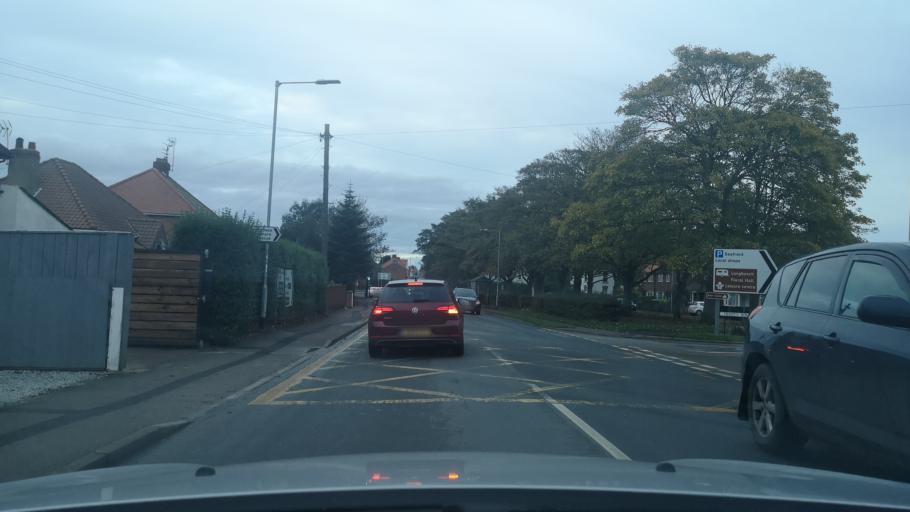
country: GB
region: England
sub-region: East Riding of Yorkshire
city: Hornsea
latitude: 53.9031
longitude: -0.1701
